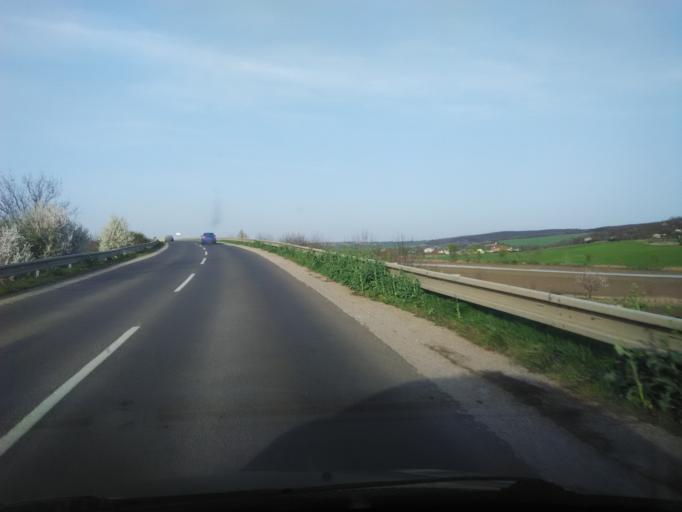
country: SK
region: Nitriansky
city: Surany
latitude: 48.0969
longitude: 18.3129
